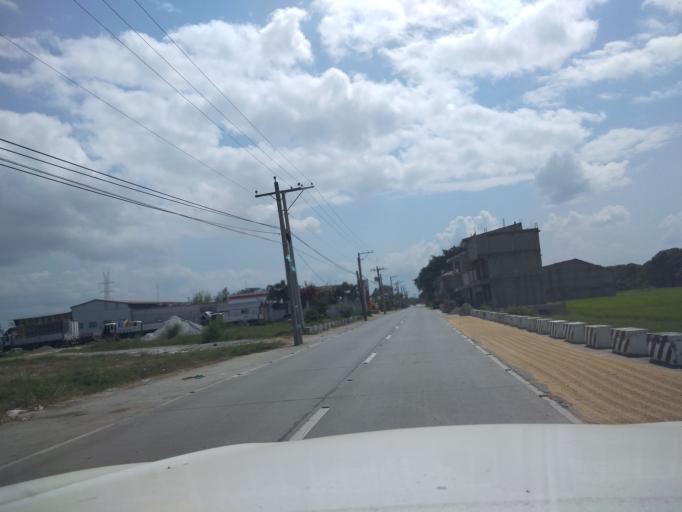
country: PH
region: Central Luzon
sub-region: Province of Pampanga
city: Talang
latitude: 15.0245
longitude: 120.8417
